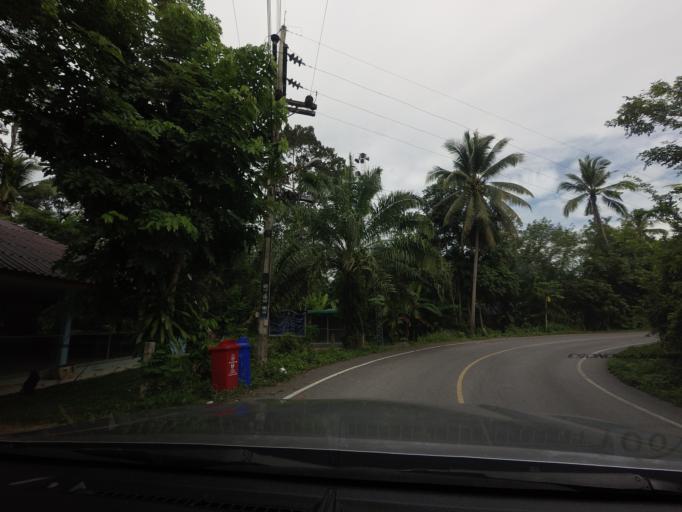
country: TH
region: Nakhon Si Thammarat
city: Phra Phrom
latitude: 8.2820
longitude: 99.9337
